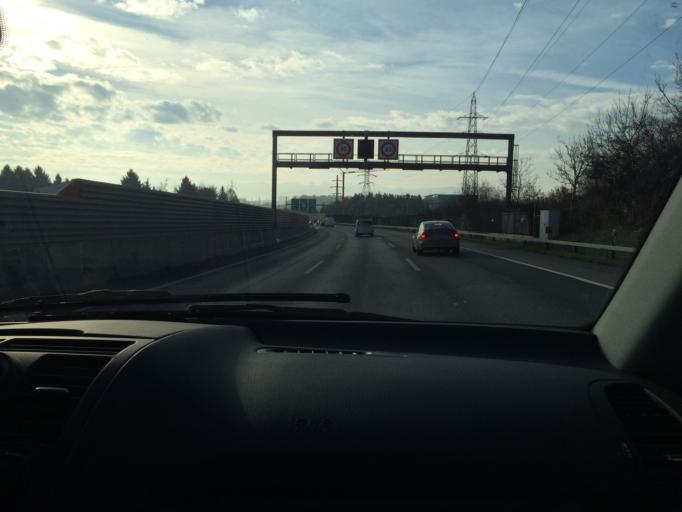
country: CH
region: Bern
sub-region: Bern-Mittelland District
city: Zollikofen
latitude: 46.9830
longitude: 7.4667
